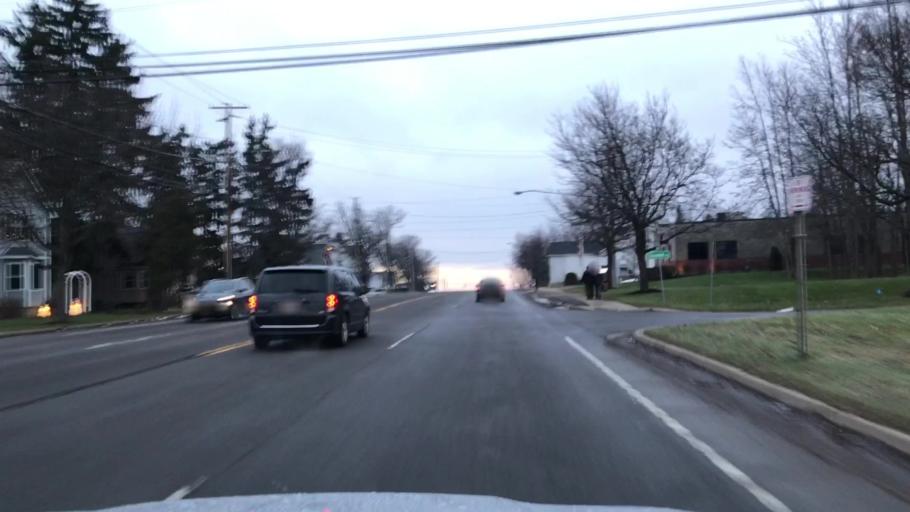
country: US
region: New York
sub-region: Erie County
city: Blasdell
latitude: 42.7940
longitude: -78.7940
